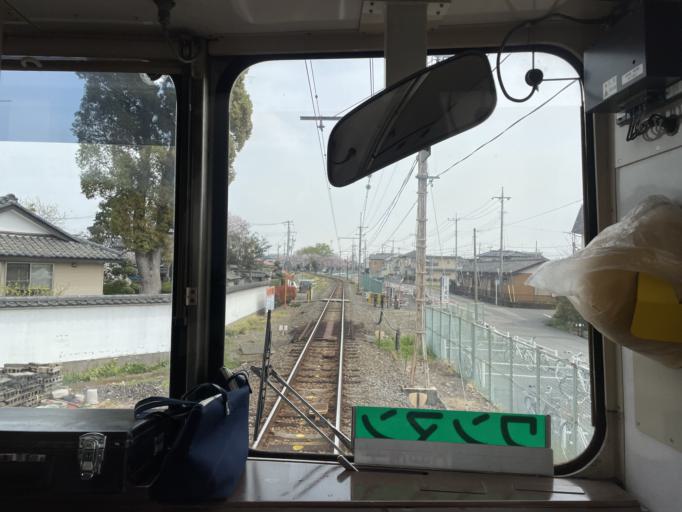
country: JP
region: Saitama
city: Gyoda
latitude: 36.1380
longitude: 139.4429
